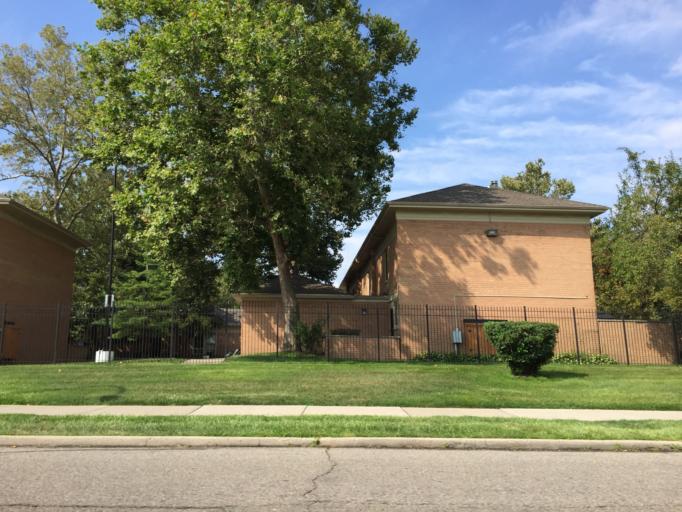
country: US
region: Michigan
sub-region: Wayne County
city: Detroit
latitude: 42.3420
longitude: -83.0253
